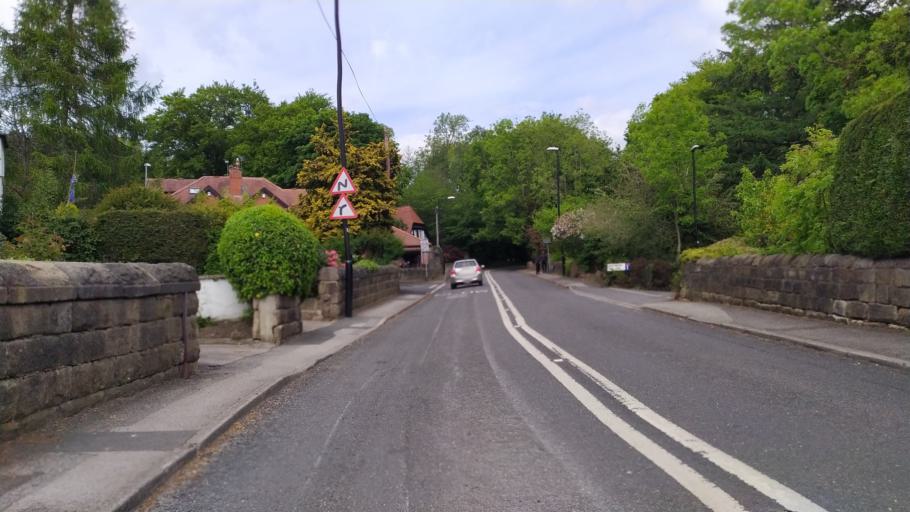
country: GB
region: England
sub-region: City and Borough of Leeds
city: Chapel Allerton
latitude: 53.8339
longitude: -1.5835
